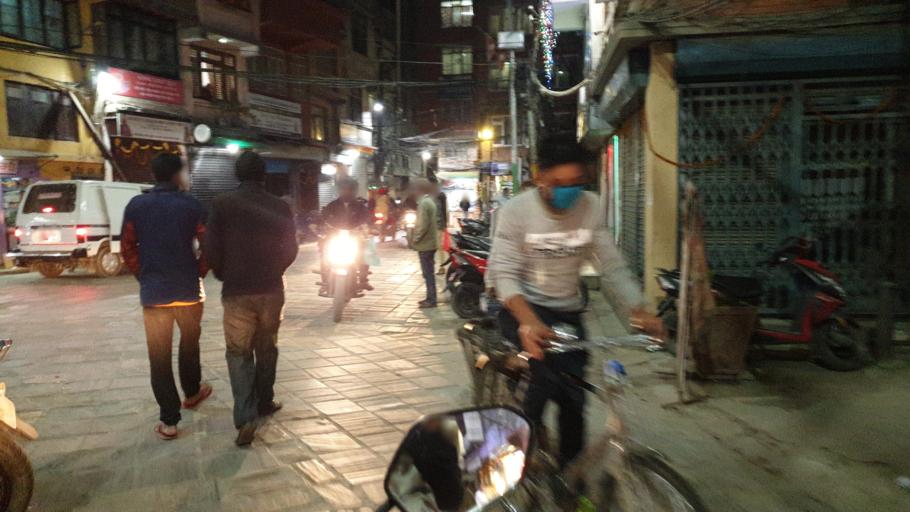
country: NP
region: Central Region
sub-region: Bagmati Zone
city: Kathmandu
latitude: 27.7020
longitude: 85.3078
